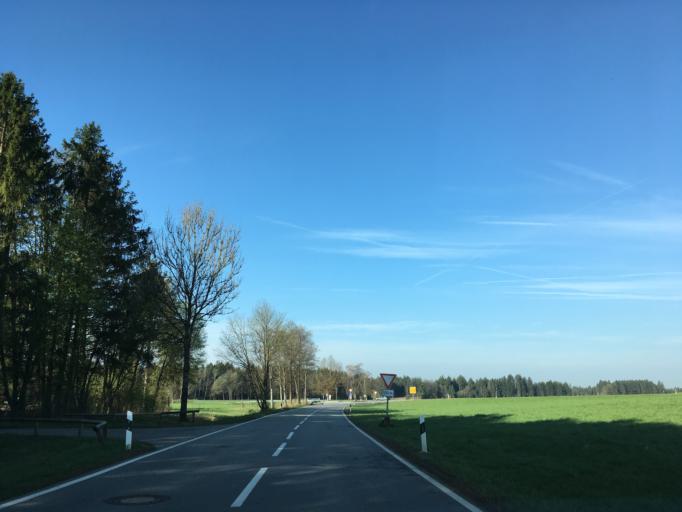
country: DE
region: Bavaria
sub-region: Upper Bavaria
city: Rohrdorf
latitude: 47.8136
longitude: 12.1878
